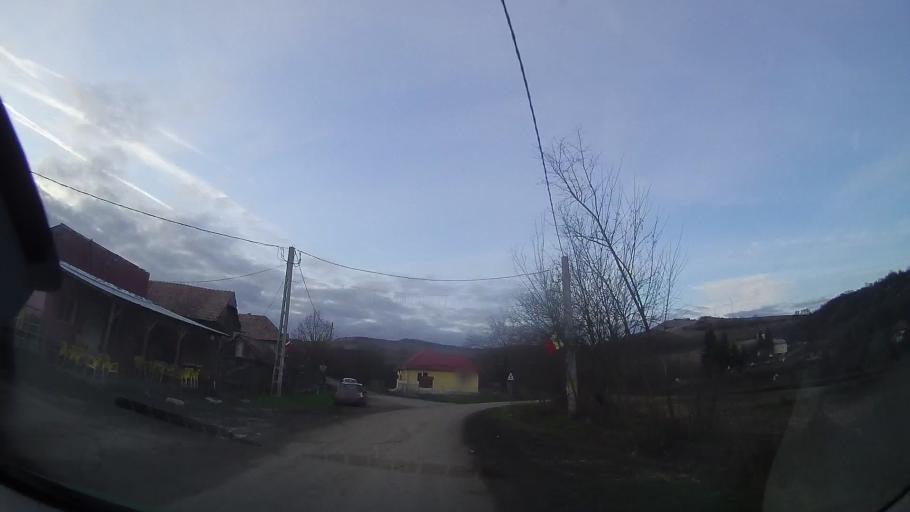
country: RO
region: Cluj
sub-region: Comuna Geaca
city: Geaca
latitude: 46.8538
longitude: 24.0477
